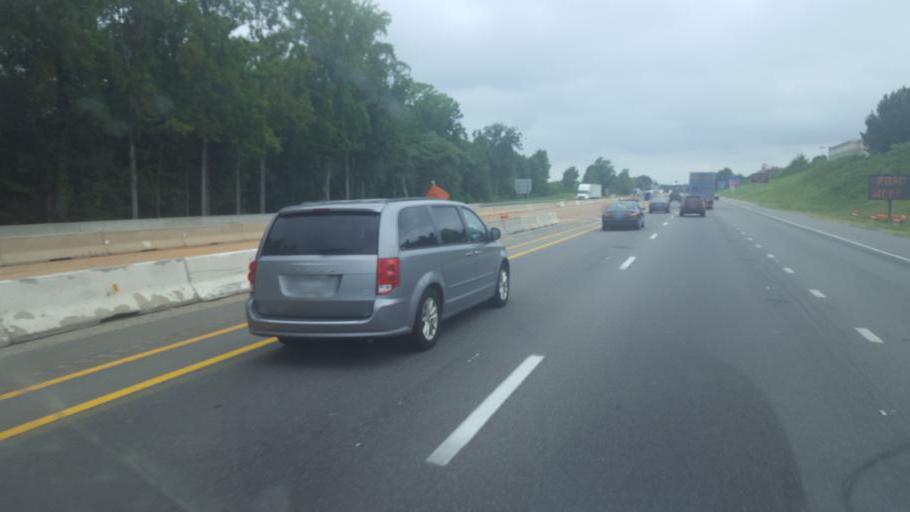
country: US
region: North Carolina
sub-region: Iredell County
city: Mooresville
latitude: 35.5853
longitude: -80.8576
